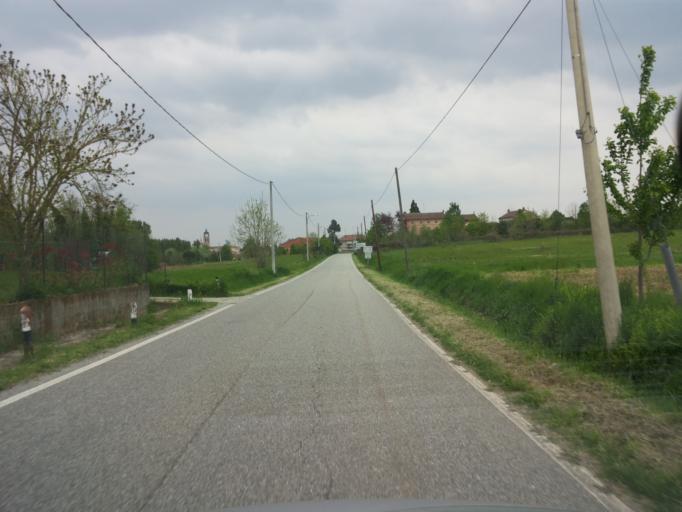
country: IT
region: Piedmont
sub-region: Provincia di Alessandria
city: Mirabello Monferrato
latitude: 45.0302
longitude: 8.5193
